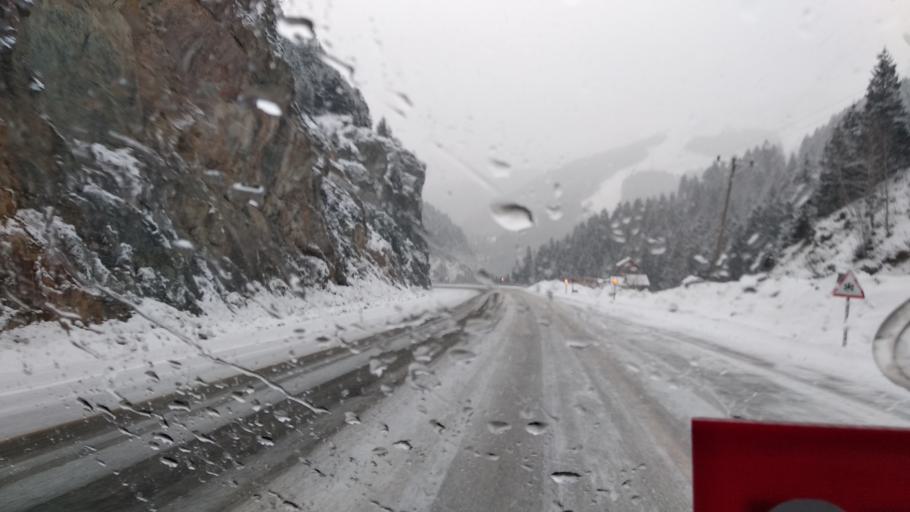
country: TR
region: Gumushane
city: Yaglidere
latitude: 40.6746
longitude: 39.4274
